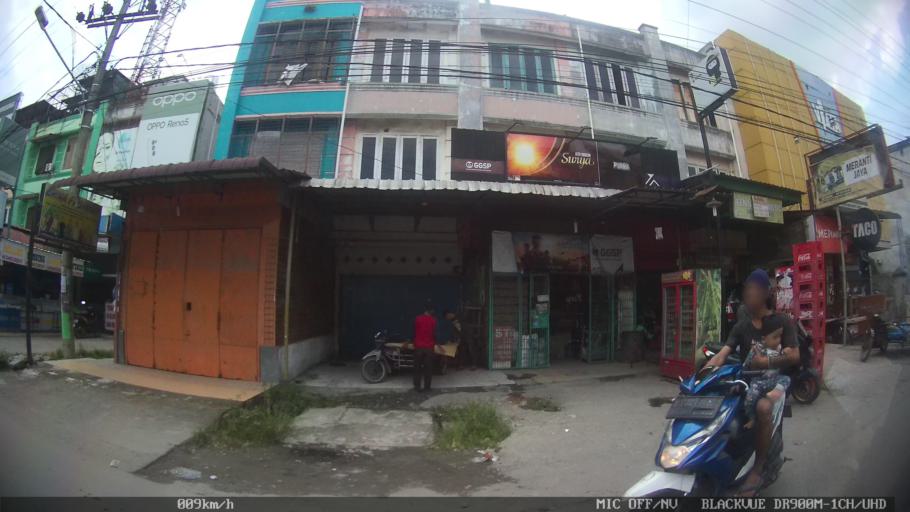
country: ID
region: North Sumatra
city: Labuhan Deli
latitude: 3.6896
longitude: 98.6575
